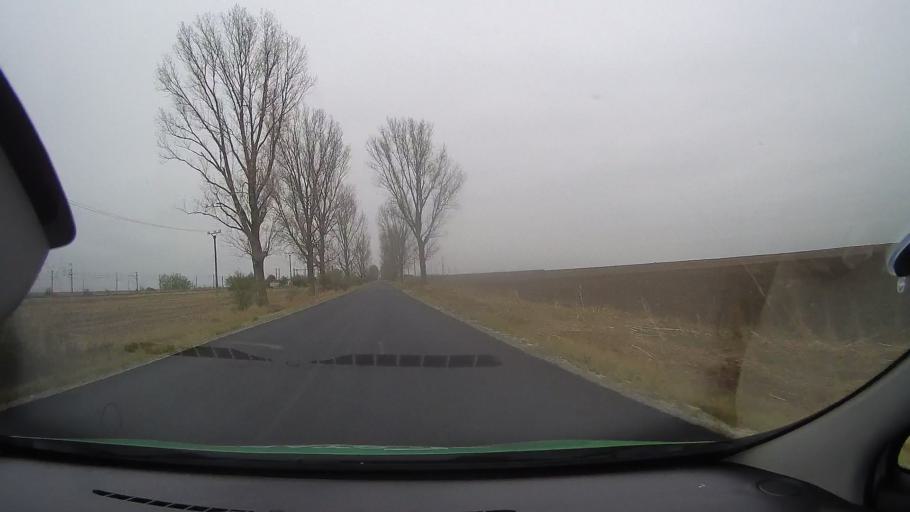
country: RO
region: Ialomita
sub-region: Comuna Valea Ciorii
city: Valea Ciorii
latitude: 44.7489
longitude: 27.5701
